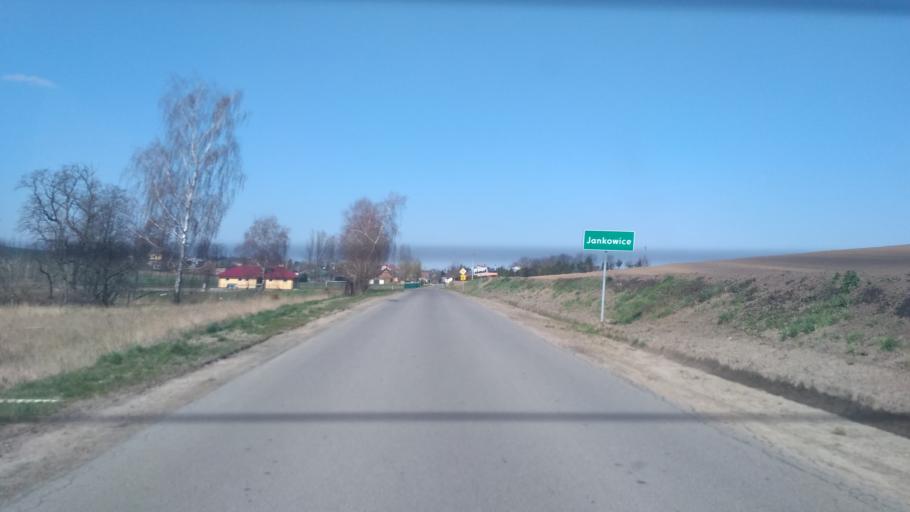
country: PL
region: Subcarpathian Voivodeship
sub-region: Powiat jaroslawski
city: Pawlosiow
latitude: 49.9541
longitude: 22.6566
